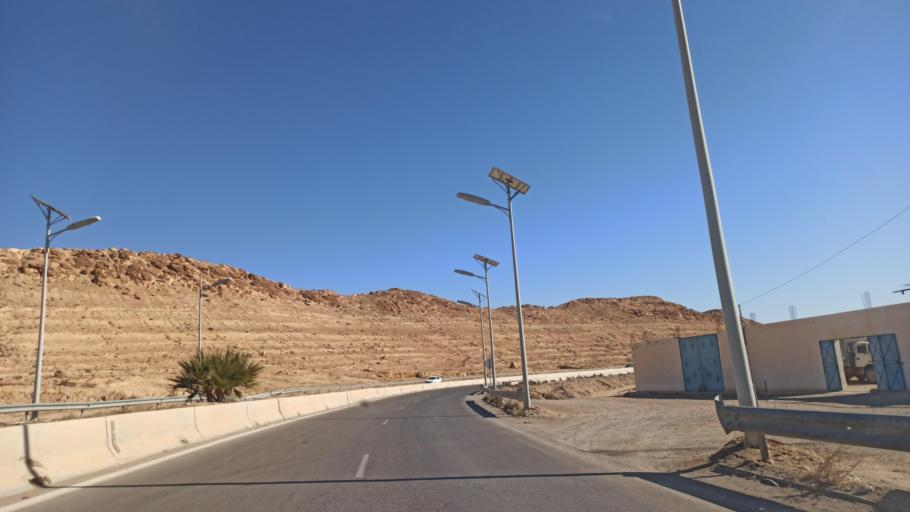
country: TN
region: Gafsa
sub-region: Gafsa Municipality
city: Gafsa
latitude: 34.4520
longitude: 8.7774
